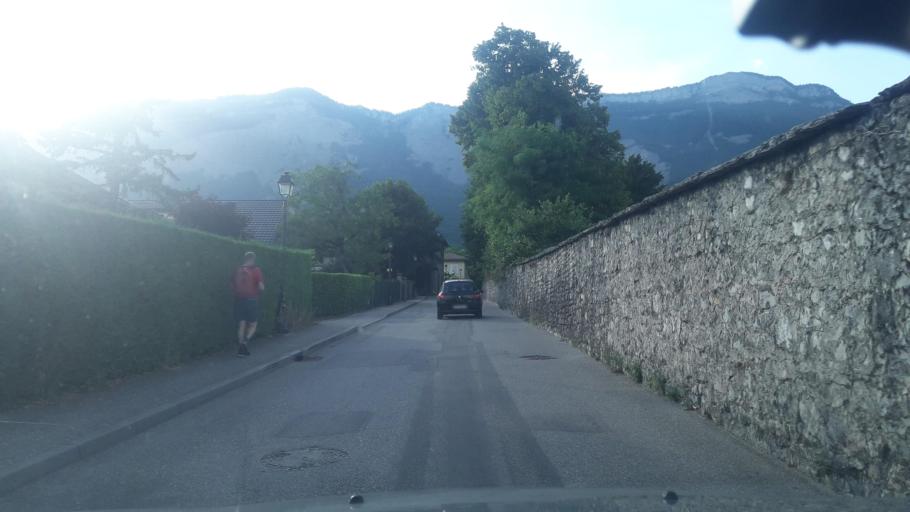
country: FR
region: Rhone-Alpes
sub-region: Departement de l'Isere
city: Saint-Ismier
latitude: 45.2464
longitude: 5.8298
